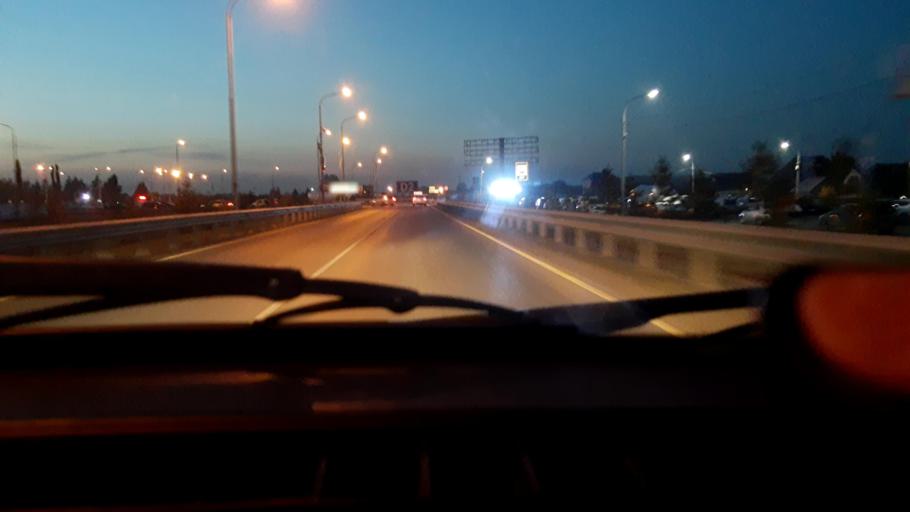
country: RU
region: Bashkortostan
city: Ufa
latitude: 54.5683
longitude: 55.8897
